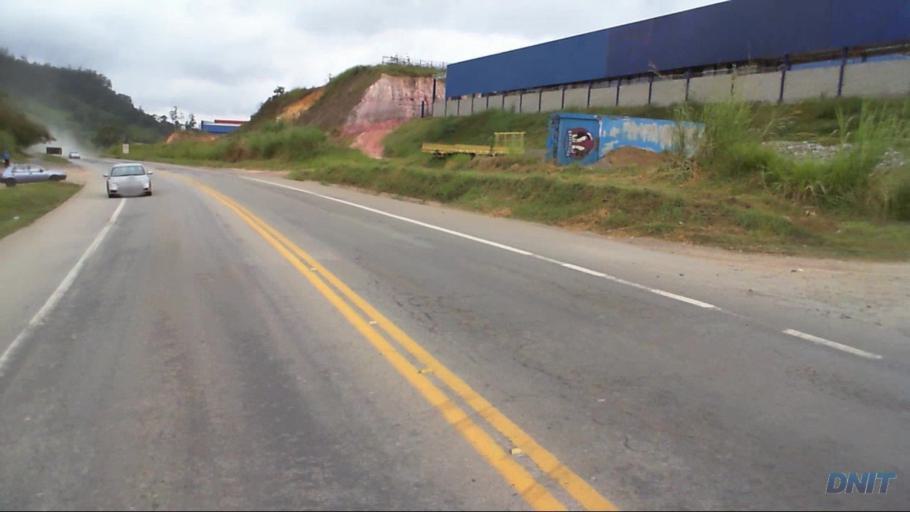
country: BR
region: Minas Gerais
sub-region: Joao Monlevade
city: Joao Monlevade
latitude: -19.8418
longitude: -43.1751
